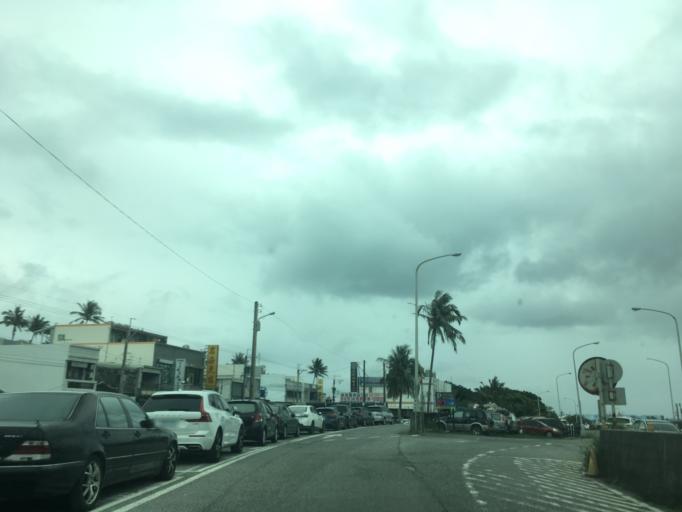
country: TW
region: Taiwan
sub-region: Taitung
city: Taitung
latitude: 22.7924
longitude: 121.1897
